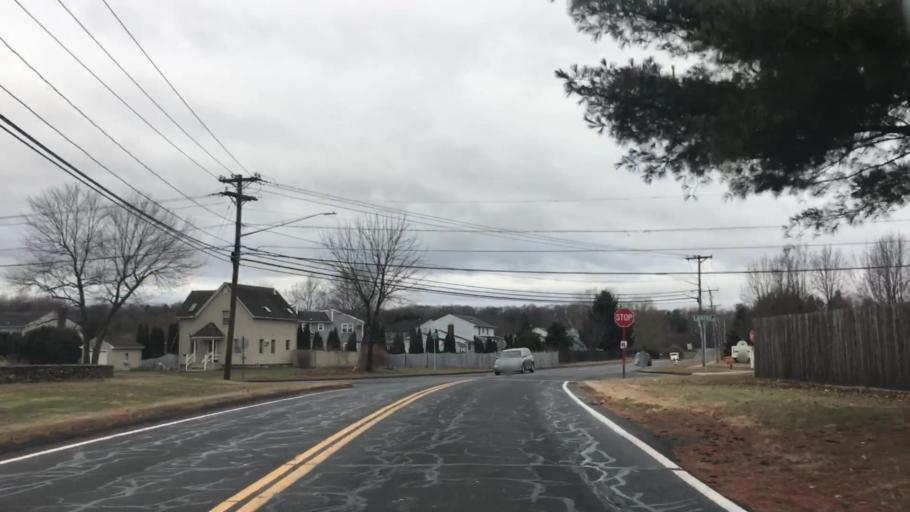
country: US
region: Connecticut
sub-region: Tolland County
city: Rockville
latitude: 41.8485
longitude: -72.5088
